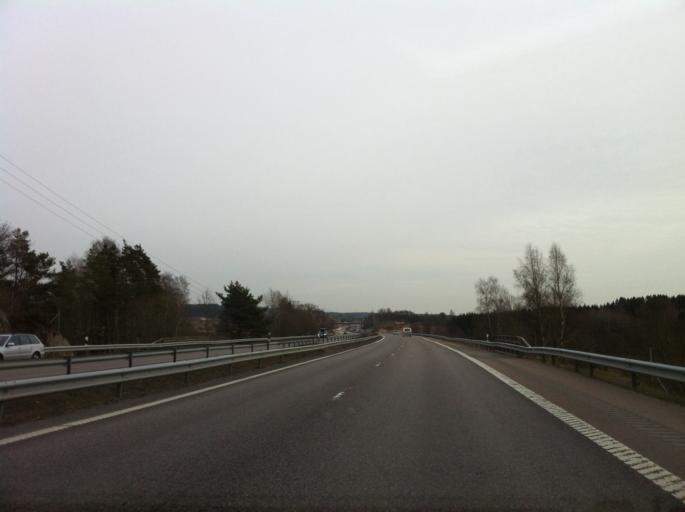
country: SE
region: Vaestra Goetaland
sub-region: Kungalvs Kommun
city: Kode
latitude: 57.9450
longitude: 11.8561
